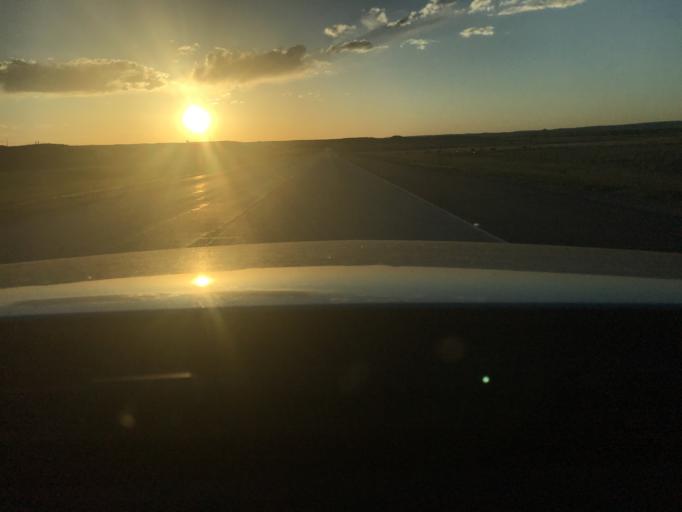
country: US
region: Wyoming
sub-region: Converse County
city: Douglas
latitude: 42.6016
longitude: -105.1055
